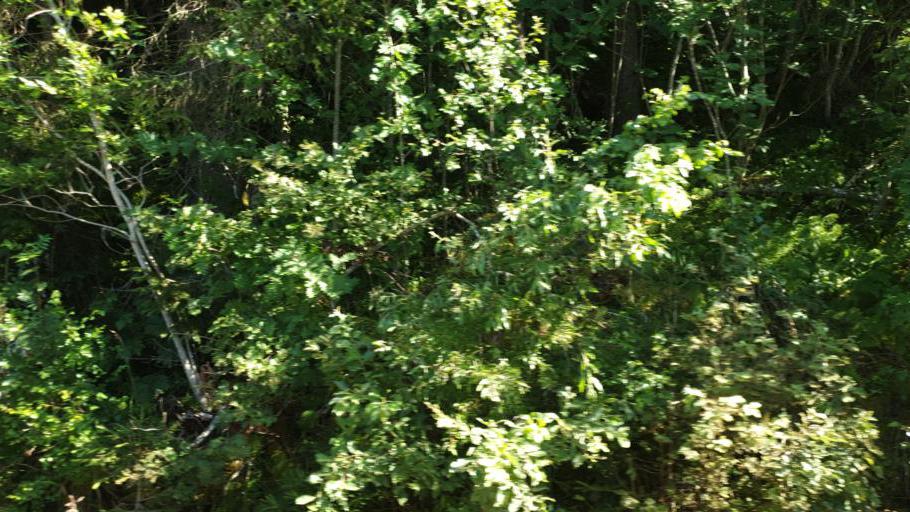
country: NO
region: Sor-Trondelag
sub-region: Orkdal
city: Orkanger
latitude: 63.1873
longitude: 9.7767
